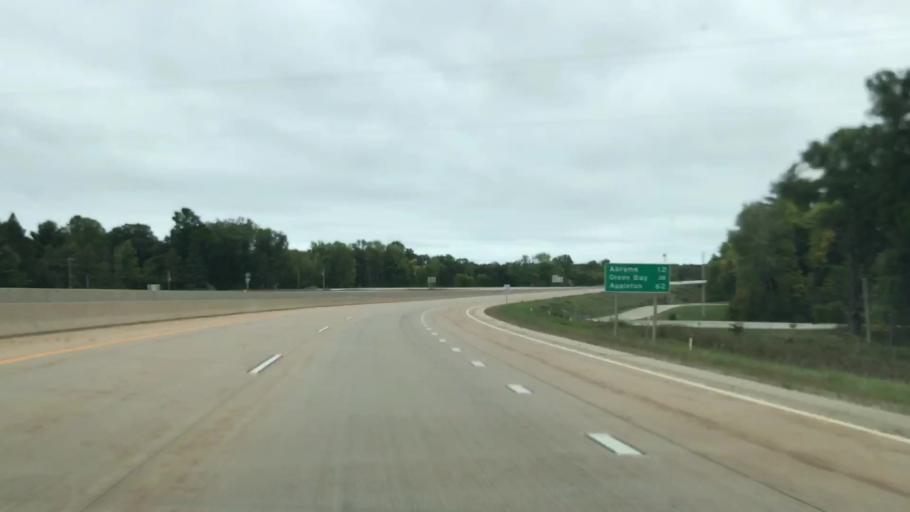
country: US
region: Wisconsin
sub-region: Oconto County
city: Oconto
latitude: 44.8910
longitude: -87.8961
